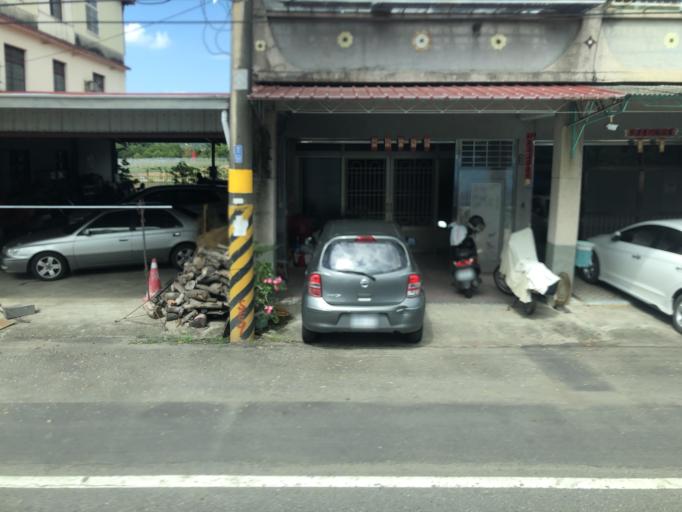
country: TW
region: Taiwan
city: Yujing
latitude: 22.9062
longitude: 120.5578
